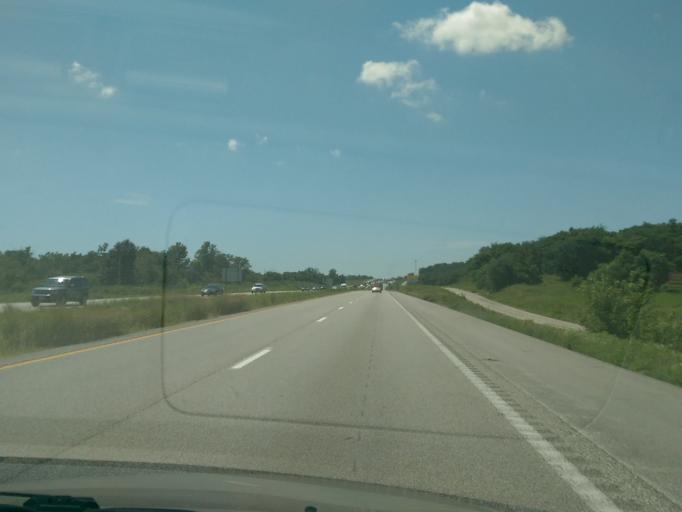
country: US
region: Missouri
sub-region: Saline County
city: Marshall
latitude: 38.9698
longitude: -93.2402
